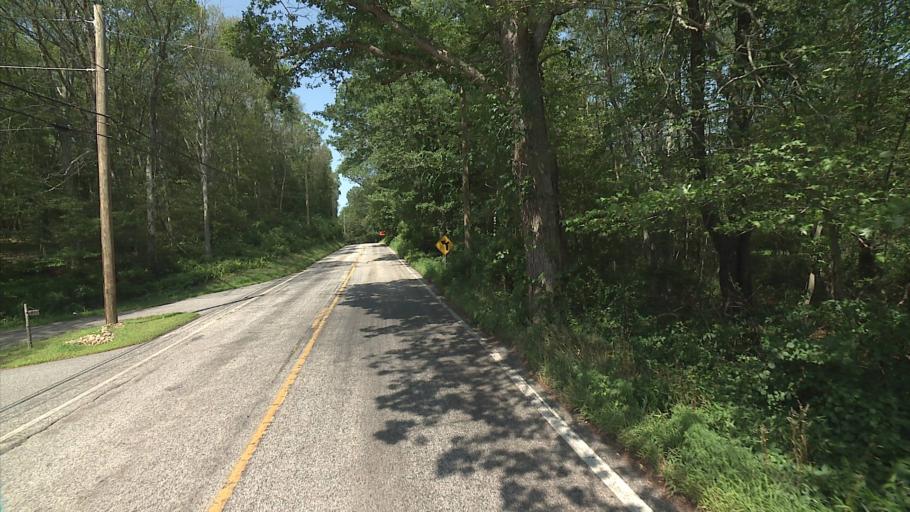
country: US
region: Connecticut
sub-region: New London County
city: Colchester
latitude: 41.5753
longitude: -72.2861
